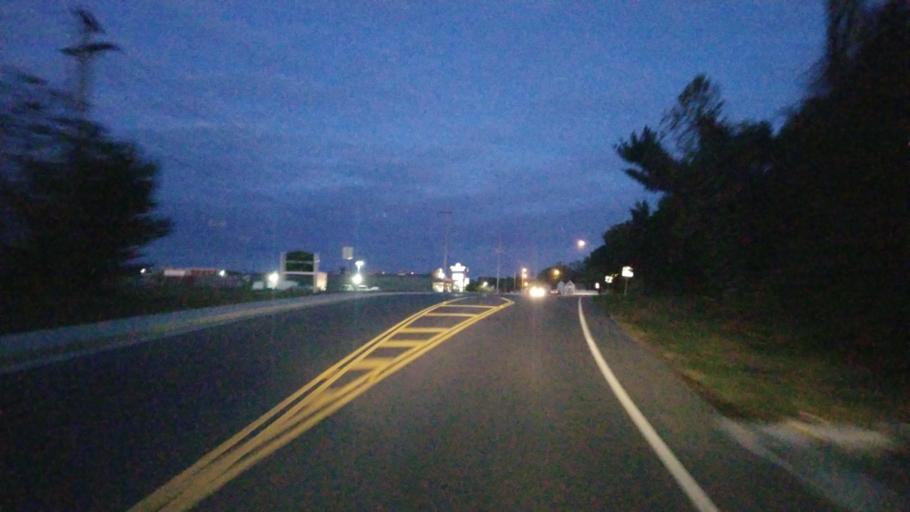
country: US
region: Ohio
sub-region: Vinton County
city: McArthur
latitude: 39.2480
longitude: -82.4877
